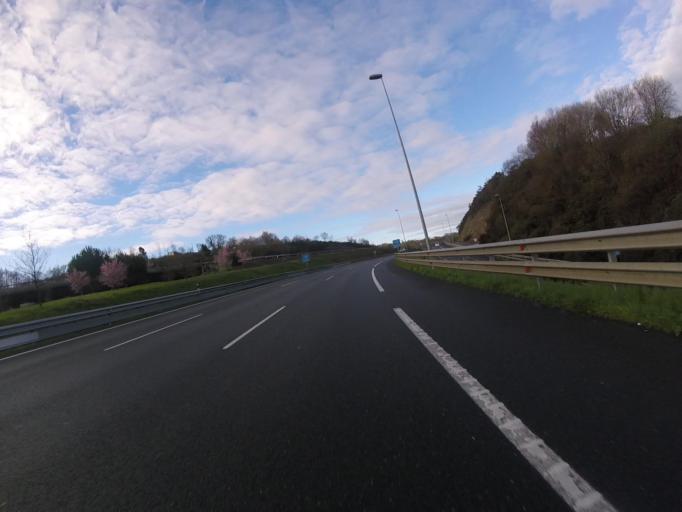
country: ES
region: Basque Country
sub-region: Provincia de Guipuzcoa
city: Errenteria
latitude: 43.3095
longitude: -1.9180
